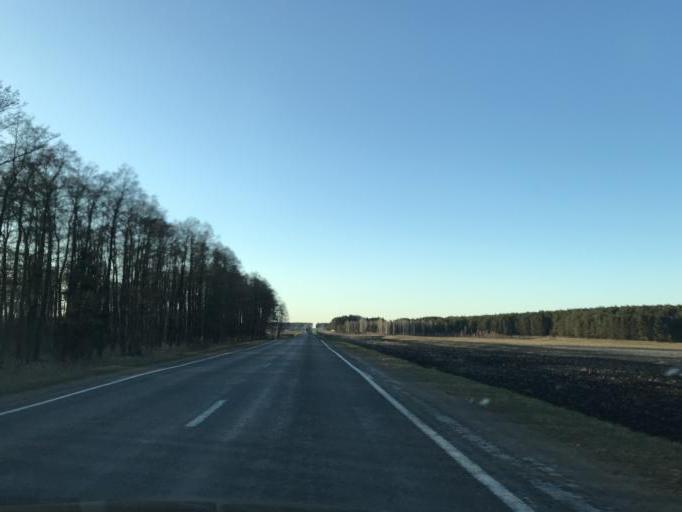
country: BY
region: Gomel
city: Buda-Kashalyova
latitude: 52.8750
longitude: 30.6795
